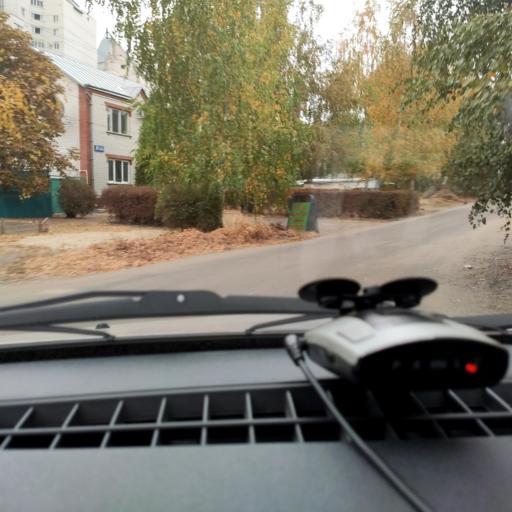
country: RU
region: Voronezj
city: Voronezh
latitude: 51.6541
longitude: 39.2369
